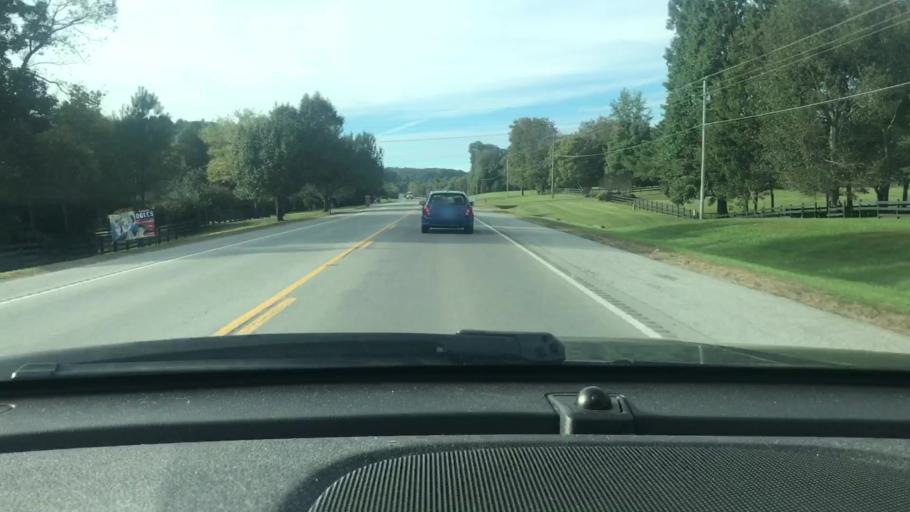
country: US
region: Tennessee
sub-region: Williamson County
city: Franklin
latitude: 35.9512
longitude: -86.9517
